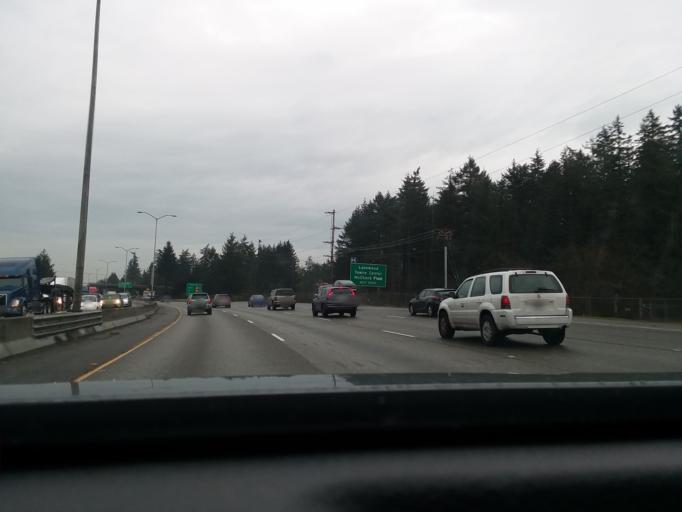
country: US
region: Washington
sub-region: Pierce County
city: McChord Air Force Base
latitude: 47.1400
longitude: -122.5182
